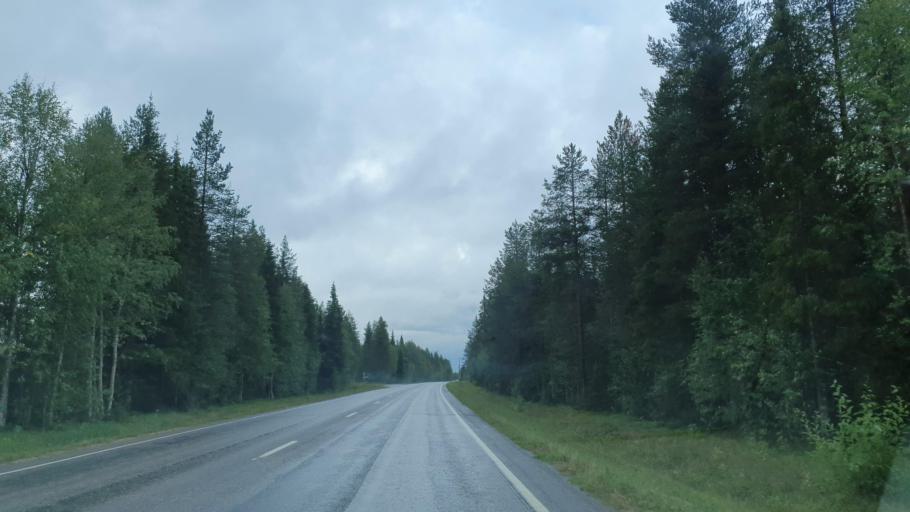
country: FI
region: Lapland
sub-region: Tunturi-Lappi
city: Kolari
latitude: 67.2664
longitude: 23.8677
